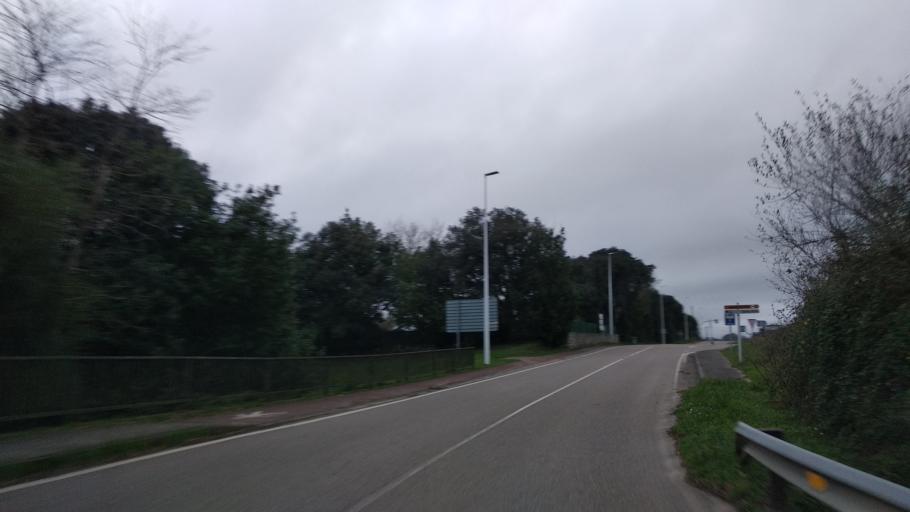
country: ES
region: Cantabria
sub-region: Provincia de Cantabria
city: Entrambasaguas
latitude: 43.4434
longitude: -3.7182
